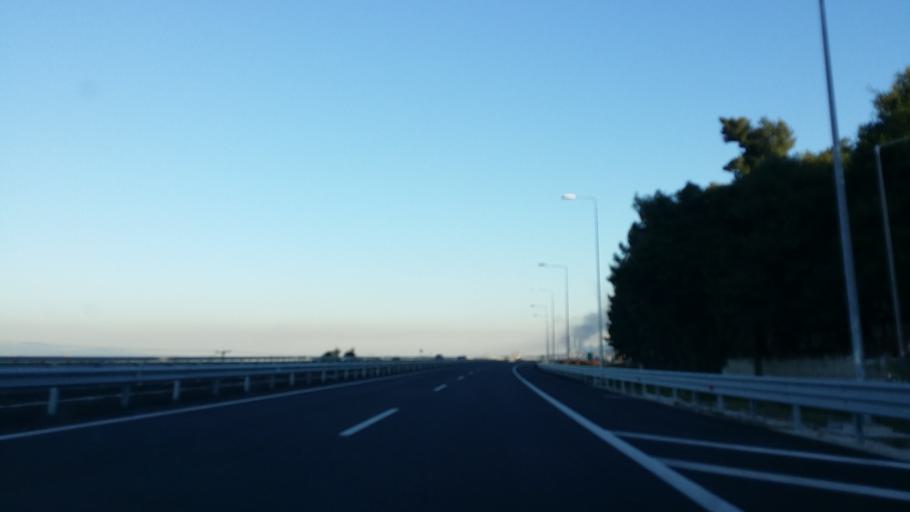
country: GR
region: Peloponnese
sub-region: Nomos Korinthias
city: Zevgolateio
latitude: 37.9211
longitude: 22.8149
